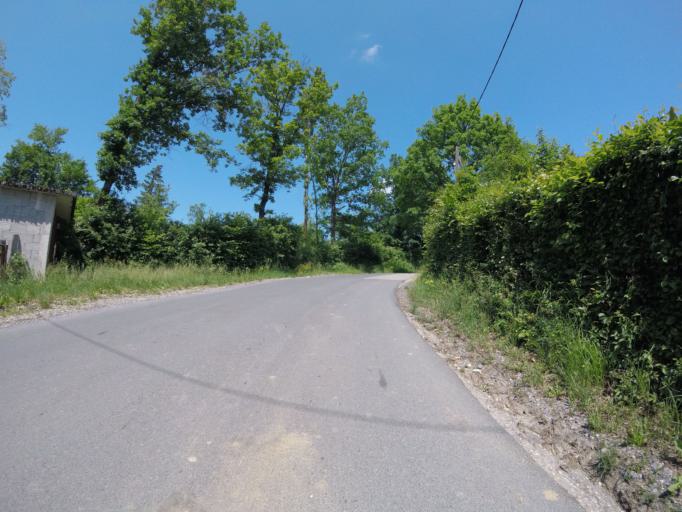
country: HR
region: Grad Zagreb
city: Strmec
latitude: 45.5705
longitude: 15.9469
